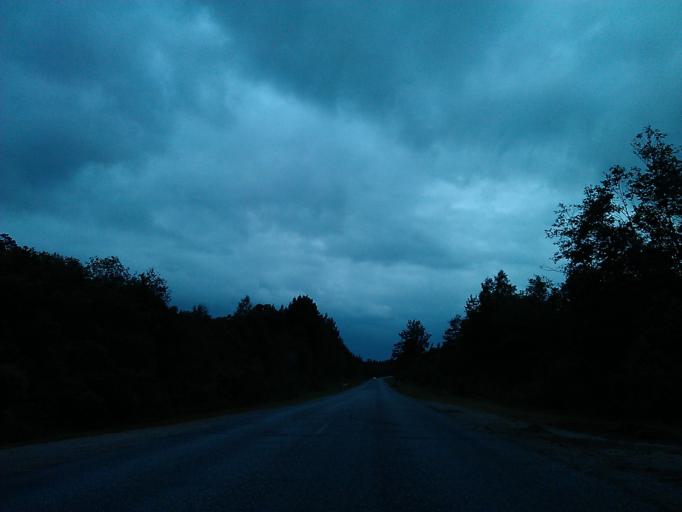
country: LV
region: Kuldigas Rajons
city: Kuldiga
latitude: 56.9898
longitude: 22.0808
